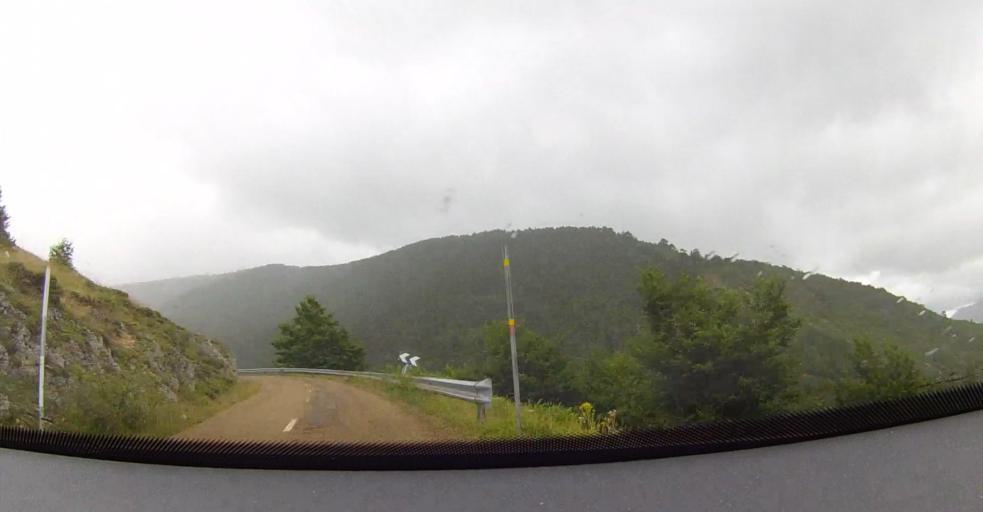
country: ES
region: Castille and Leon
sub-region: Provincia de Leon
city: Puebla de Lillo
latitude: 43.0595
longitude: -5.2766
